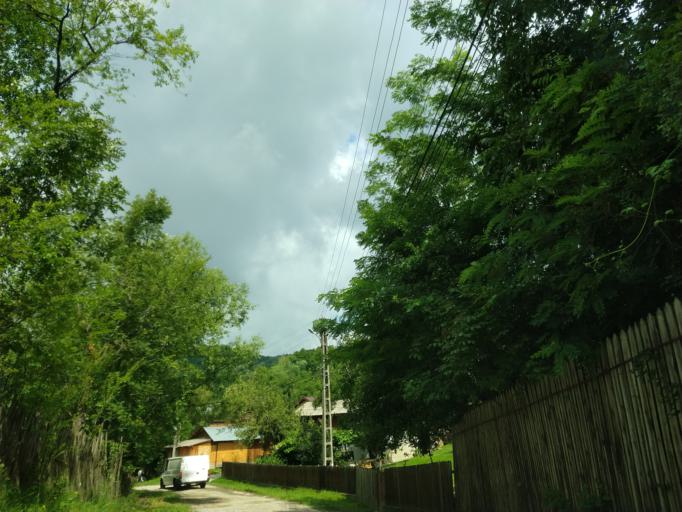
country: RO
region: Prahova
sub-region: Oras Breaza
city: Valea Tarsei
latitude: 45.1853
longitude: 25.6294
